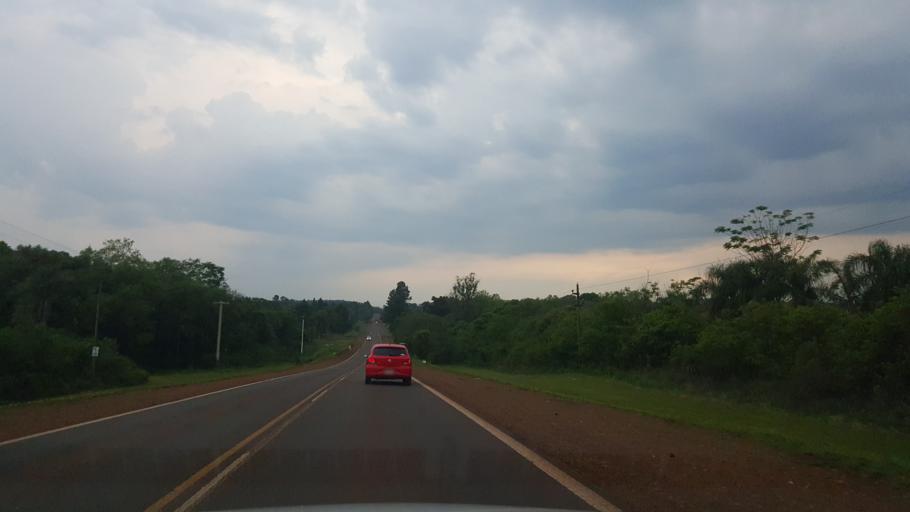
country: AR
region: Misiones
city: Gobernador Roca
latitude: -27.1759
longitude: -55.4529
